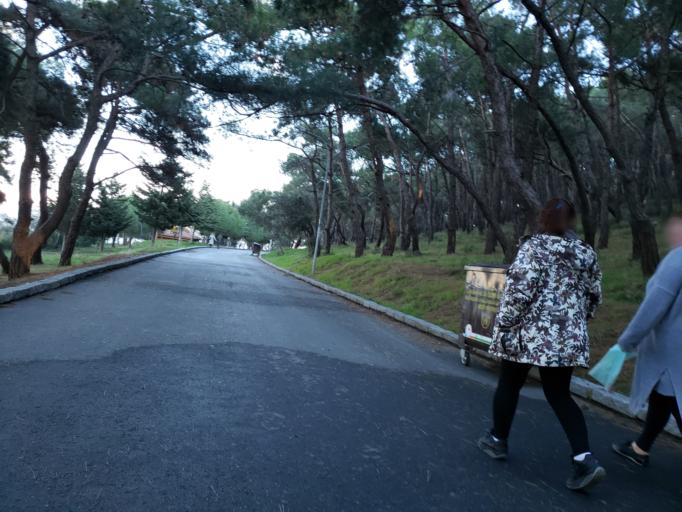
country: TR
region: Istanbul
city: Adalan
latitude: 40.8845
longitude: 29.0945
